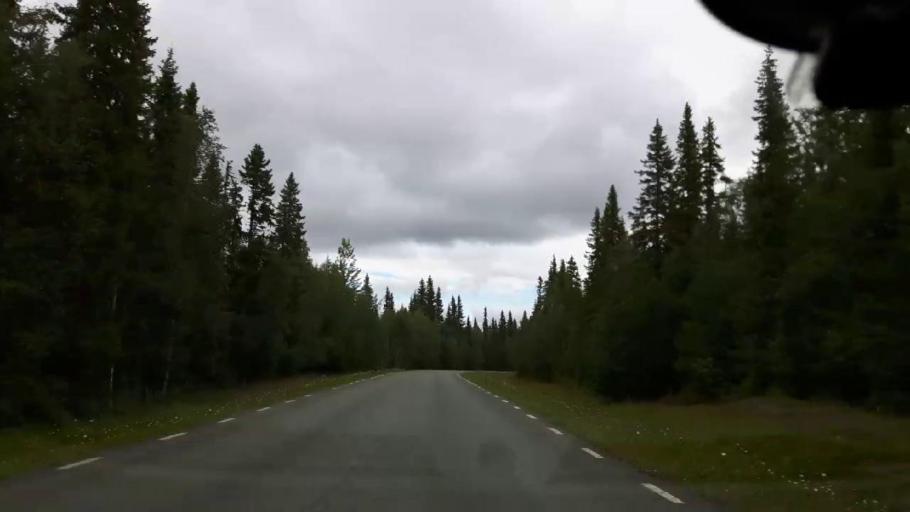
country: SE
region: Jaemtland
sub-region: Krokoms Kommun
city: Valla
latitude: 63.6101
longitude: 13.8124
